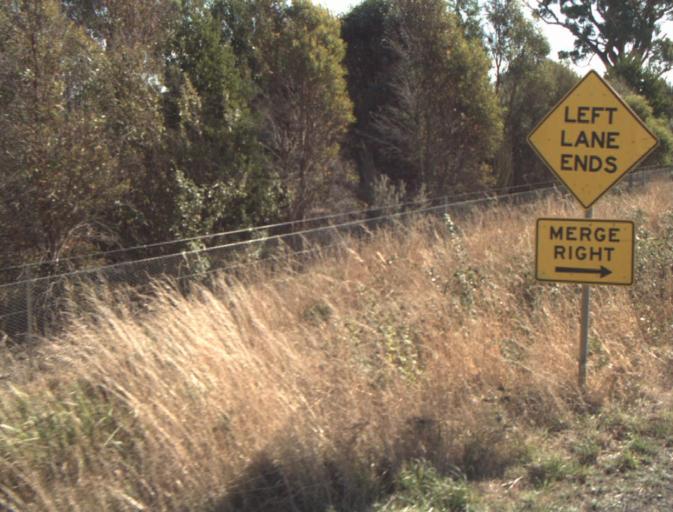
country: AU
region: Tasmania
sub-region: Launceston
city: Mayfield
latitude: -41.3414
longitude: 147.0884
